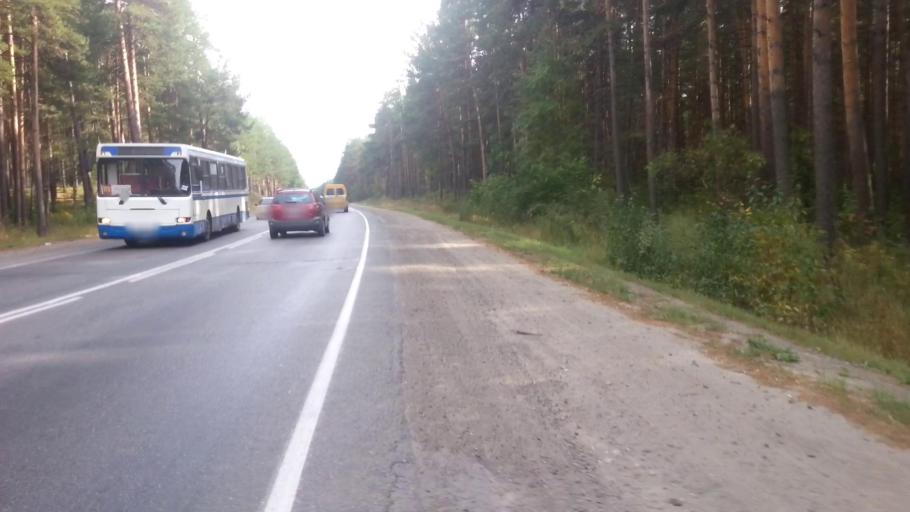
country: RU
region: Altai Krai
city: Yuzhnyy
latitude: 53.2978
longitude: 83.7031
